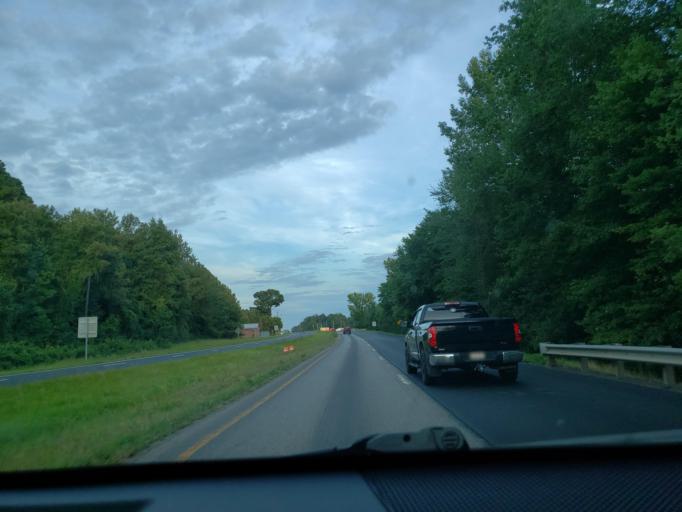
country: US
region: Virginia
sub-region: City of Emporia
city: Emporia
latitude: 36.7105
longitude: -77.5695
